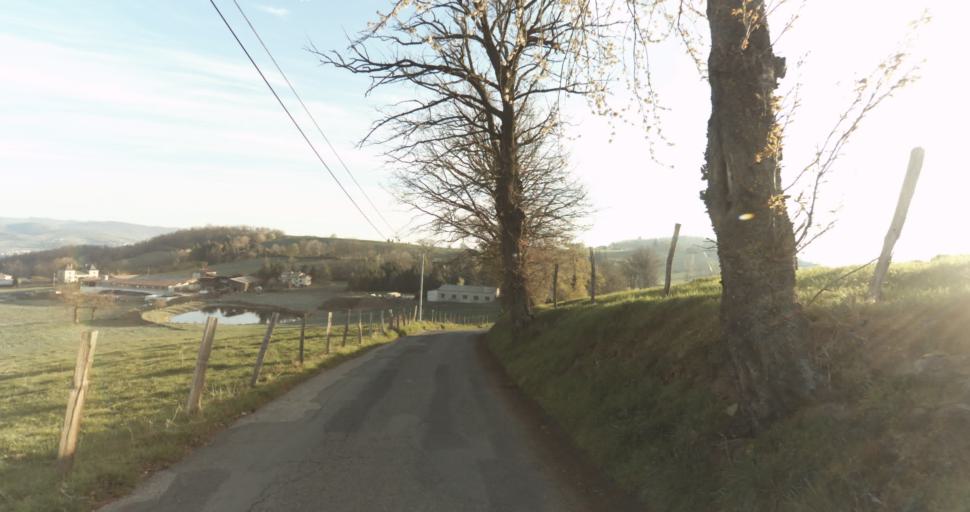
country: FR
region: Rhone-Alpes
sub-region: Departement de la Loire
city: Saint-Jean-Bonnefonds
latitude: 45.4573
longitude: 4.4377
